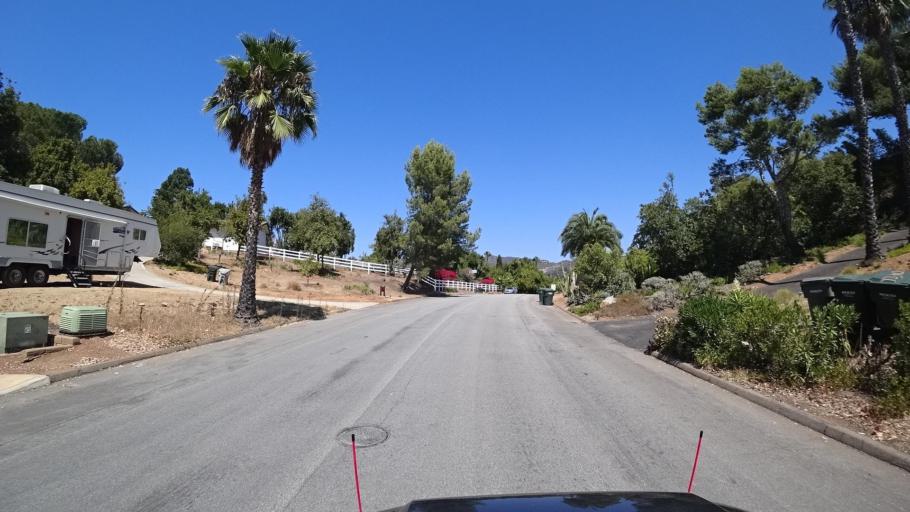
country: US
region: California
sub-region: San Diego County
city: San Marcos
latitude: 33.1878
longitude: -117.1897
